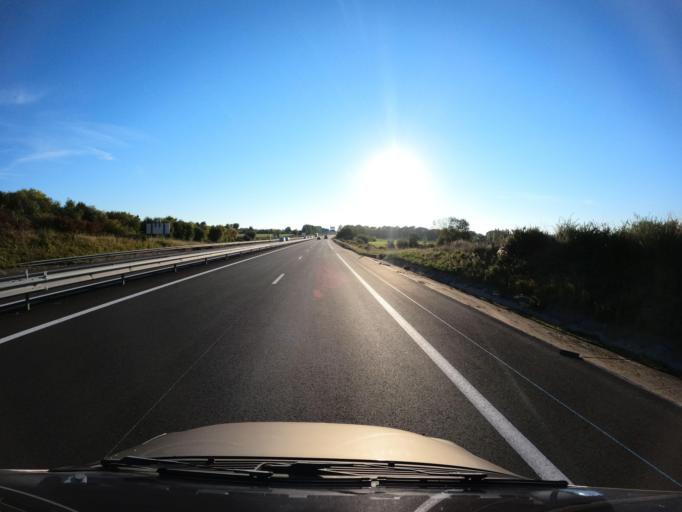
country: FR
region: Pays de la Loire
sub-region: Departement de la Vendee
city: Saint-Fulgent
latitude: 46.8167
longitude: -1.1874
